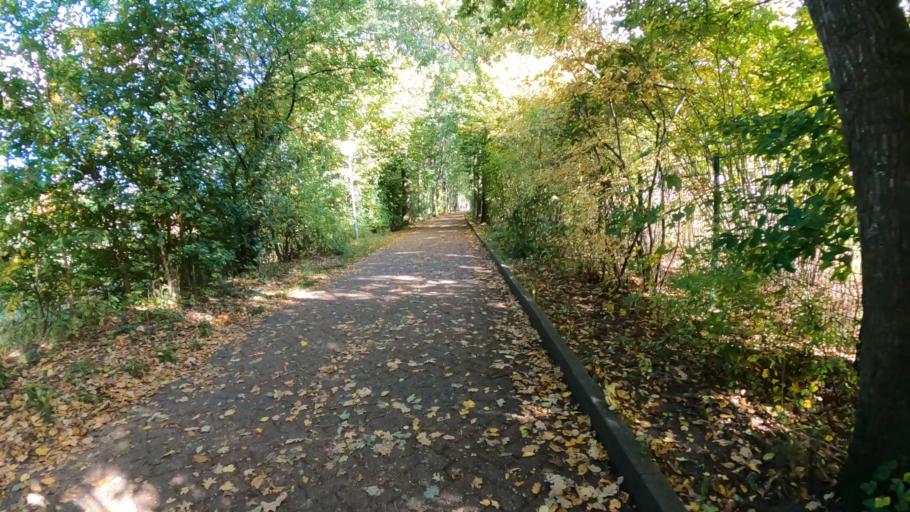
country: DE
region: Schleswig-Holstein
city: Henstedt-Ulzburg
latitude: 53.7921
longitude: 9.9938
